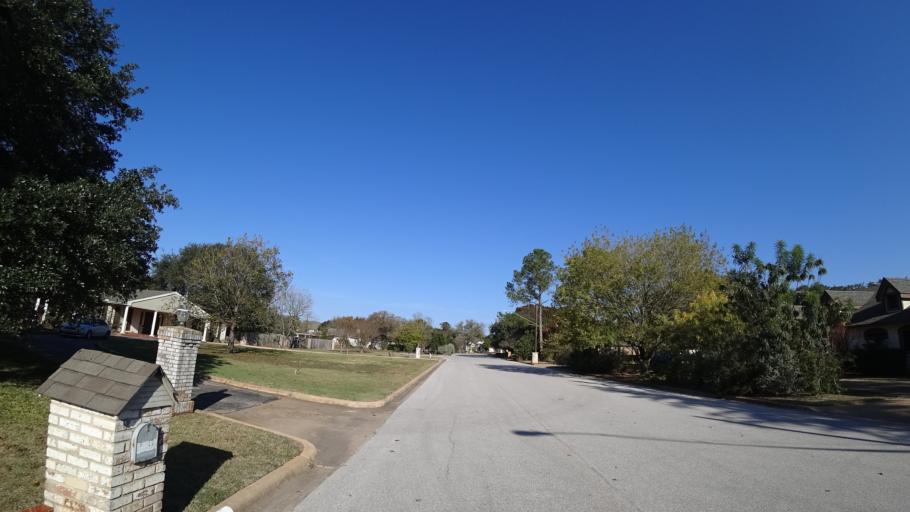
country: US
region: Texas
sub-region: Travis County
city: Shady Hollow
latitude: 30.2219
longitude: -97.8497
